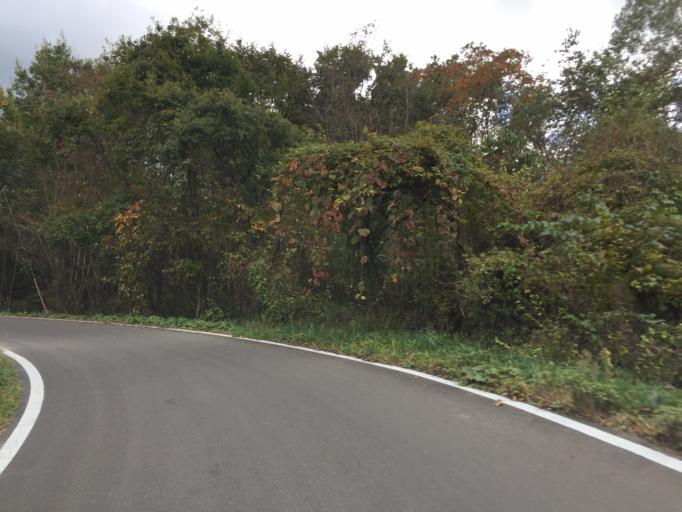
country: JP
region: Miyagi
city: Marumori
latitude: 37.8104
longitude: 140.7805
